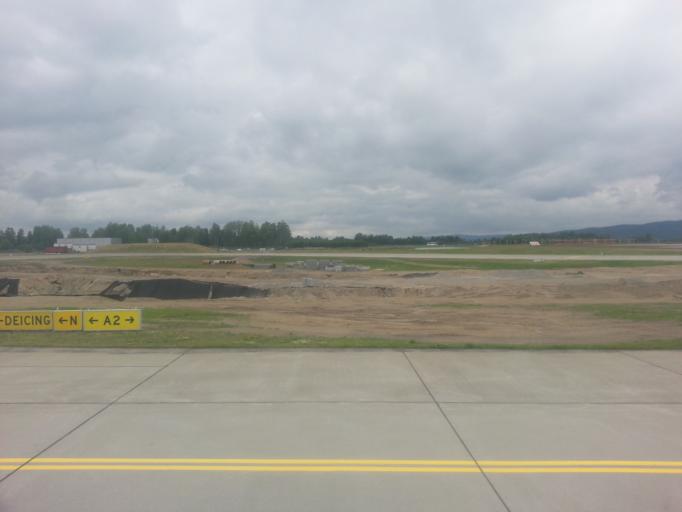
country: NO
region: Akershus
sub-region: Nannestad
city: Teigebyen
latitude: 60.1855
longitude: 11.0776
